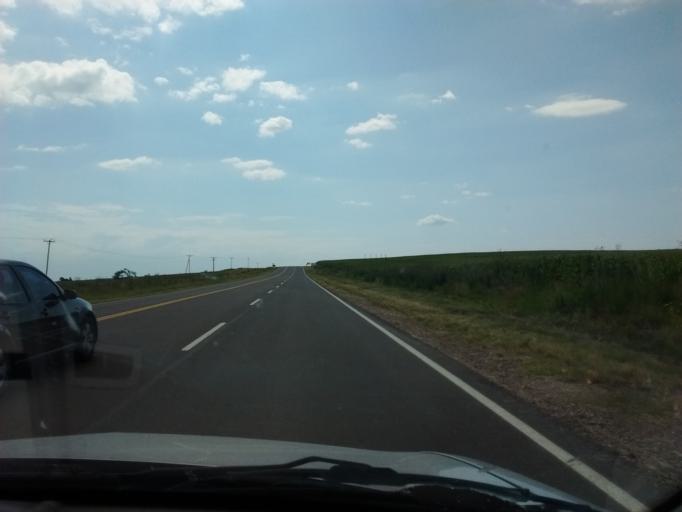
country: AR
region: Entre Rios
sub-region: Departamento de Victoria
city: Victoria
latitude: -32.6490
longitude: -60.0880
